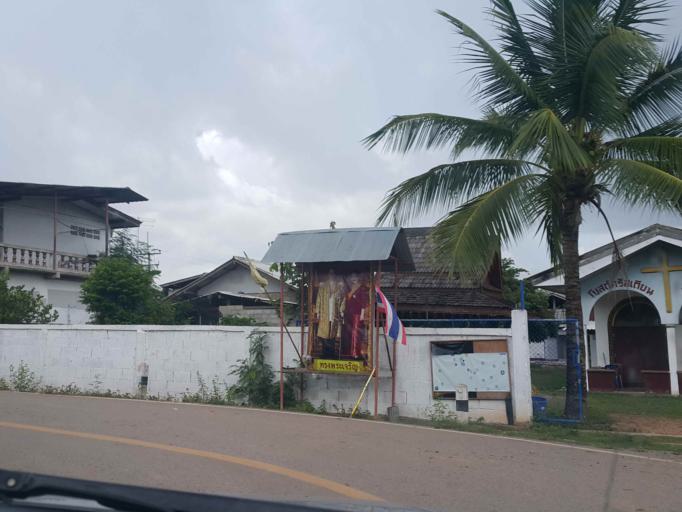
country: TH
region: Phayao
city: Dok Kham Tai
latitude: 19.0375
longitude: 99.9541
